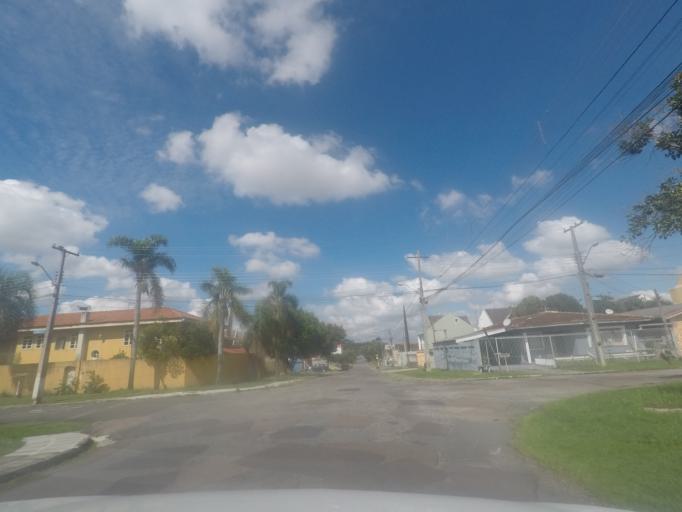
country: BR
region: Parana
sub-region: Pinhais
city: Pinhais
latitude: -25.4703
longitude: -49.2277
